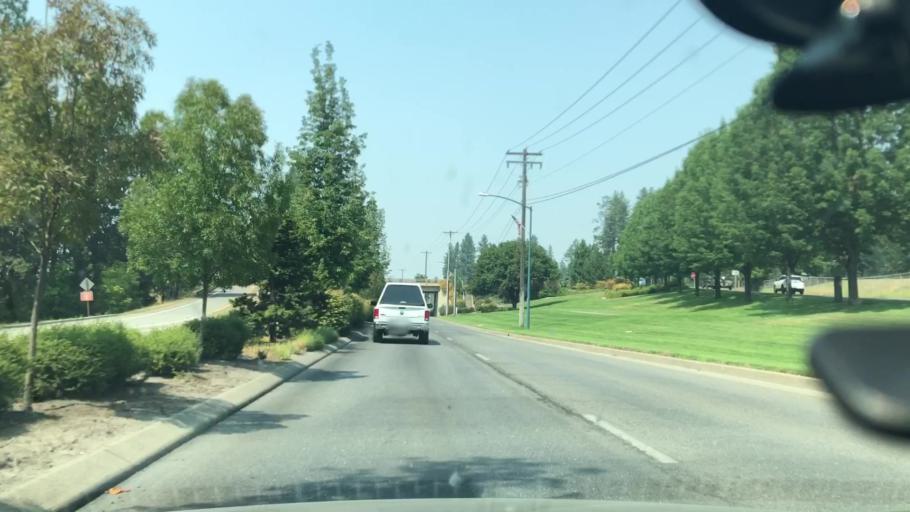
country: US
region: Idaho
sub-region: Kootenai County
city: Coeur d'Alene
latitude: 47.6857
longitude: -116.7954
